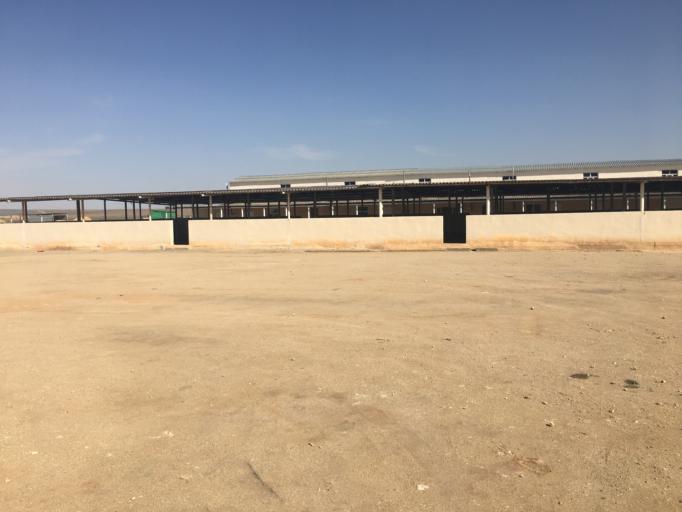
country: TM
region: Balkan
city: Balkanabat
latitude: 40.3351
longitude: 54.4879
